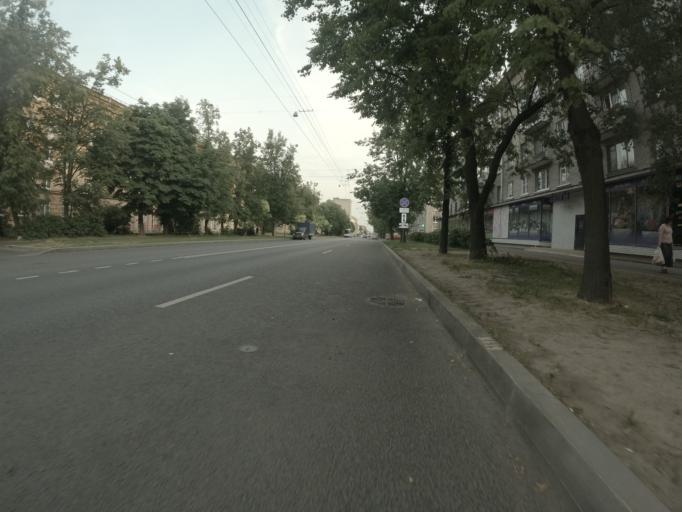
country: RU
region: Leningrad
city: Kalininskiy
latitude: 59.9764
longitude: 30.3917
